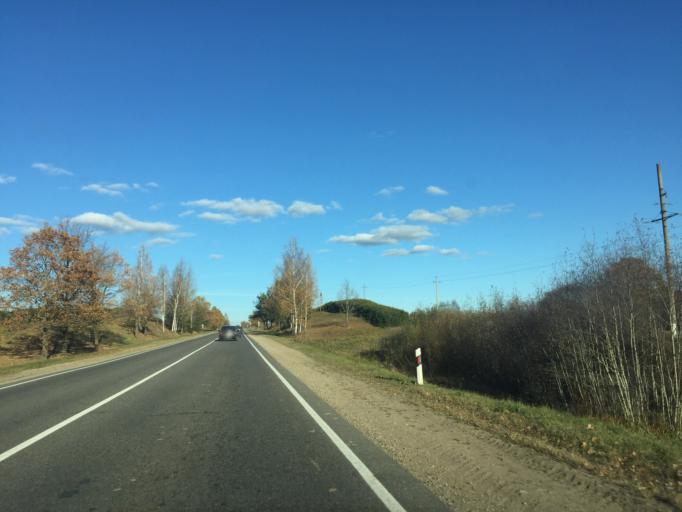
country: BY
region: Vitebsk
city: Dzisna
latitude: 55.2527
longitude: 28.1086
